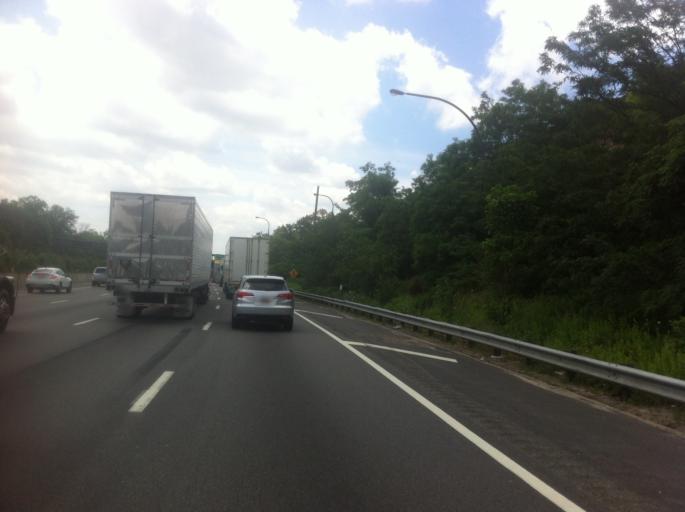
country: US
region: New York
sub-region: Nassau County
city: Manhasset Hills
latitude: 40.7673
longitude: -73.6979
